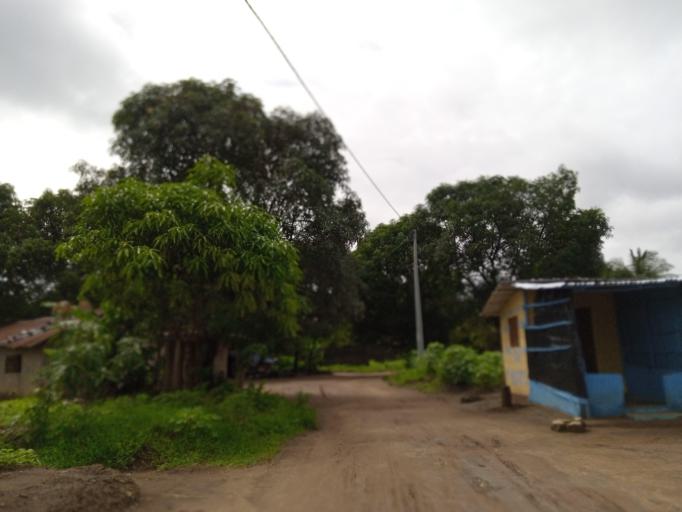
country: SL
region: Northern Province
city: Sawkta
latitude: 8.6258
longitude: -13.2039
